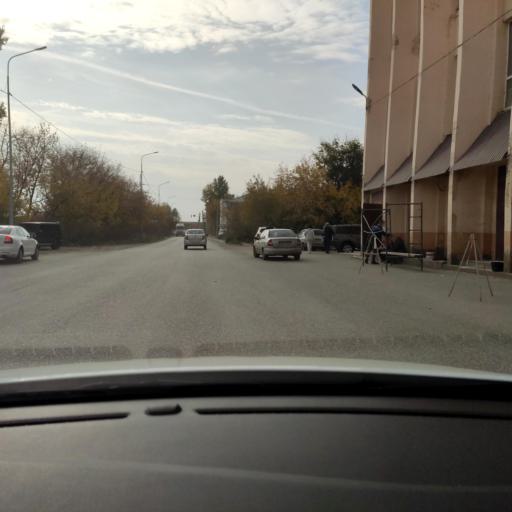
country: RU
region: Tatarstan
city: Verkhniy Uslon
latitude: 55.8004
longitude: 49.0440
